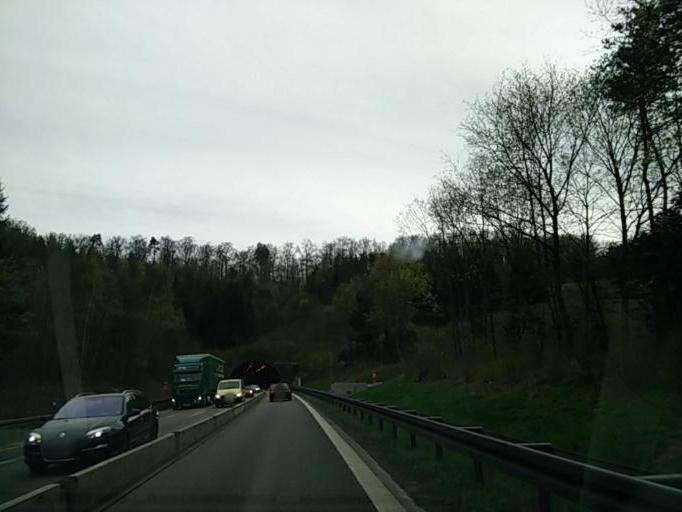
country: DE
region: Baden-Wuerttemberg
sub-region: Regierungsbezirk Stuttgart
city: Nufringen
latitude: 48.6084
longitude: 8.8983
